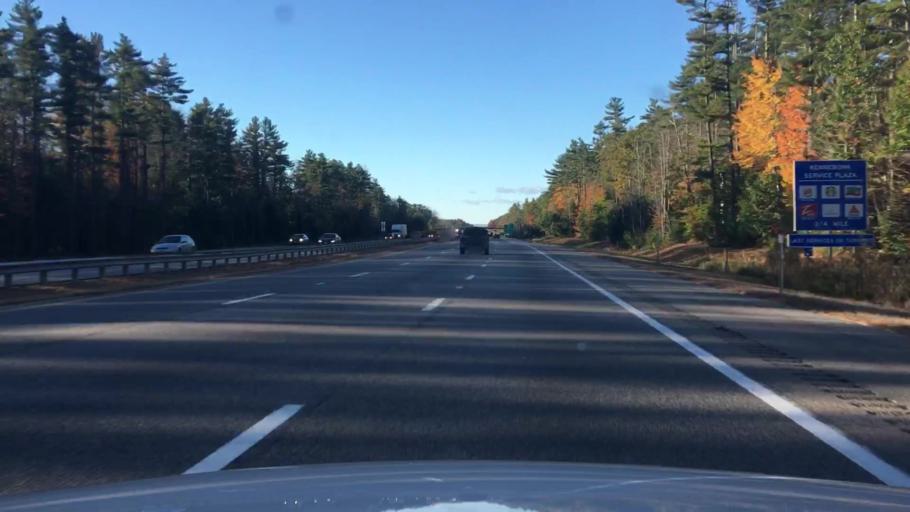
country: US
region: Maine
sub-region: York County
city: West Kennebunk
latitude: 43.4236
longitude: -70.5524
